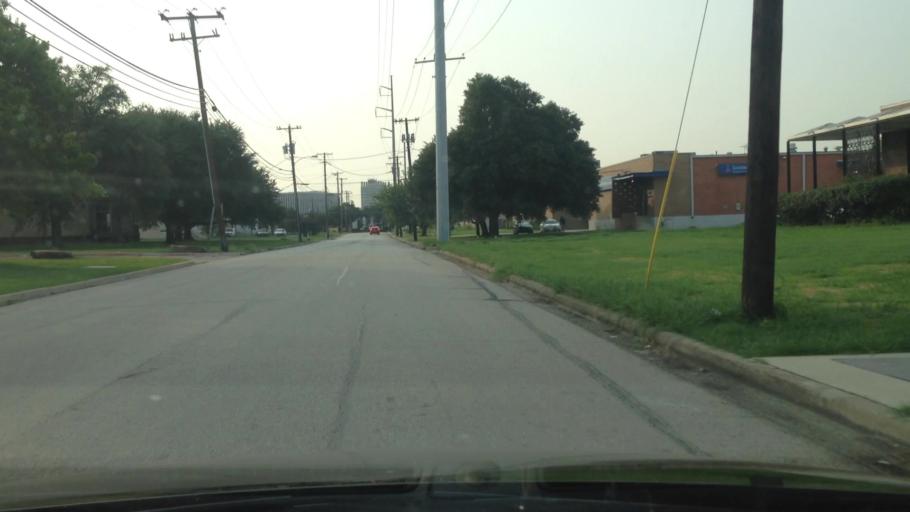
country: US
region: Texas
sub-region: Dallas County
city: Irving
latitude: 32.8258
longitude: -96.8792
